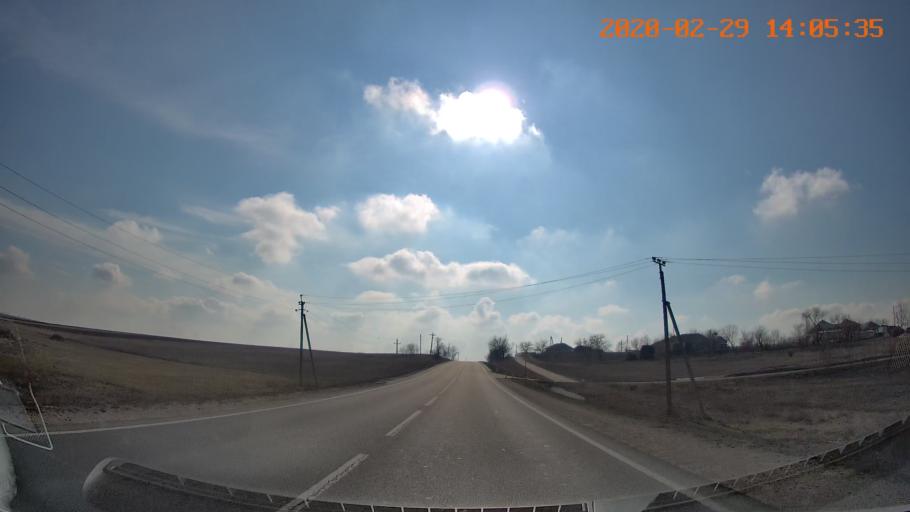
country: MD
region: Floresti
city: Leninskiy
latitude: 47.6784
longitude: 28.4974
